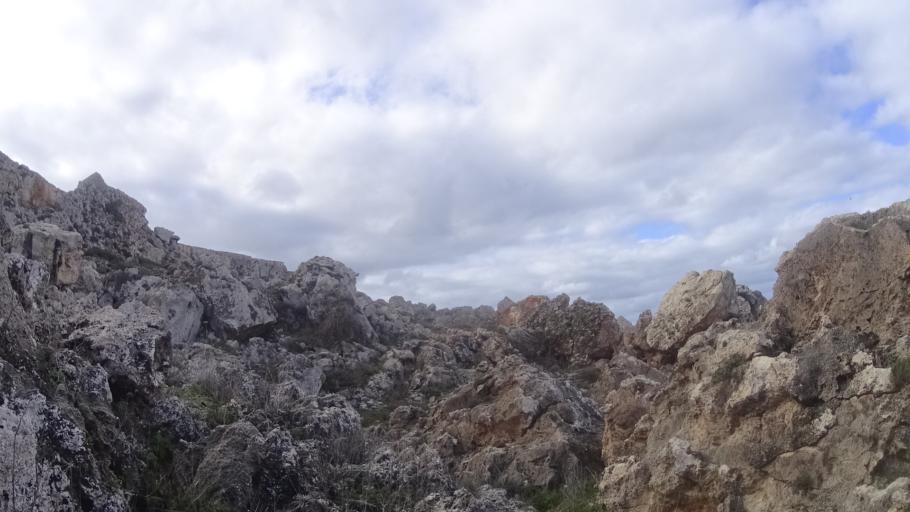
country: MT
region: Il-Mellieha
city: Mellieha
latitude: 35.9792
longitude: 14.3281
